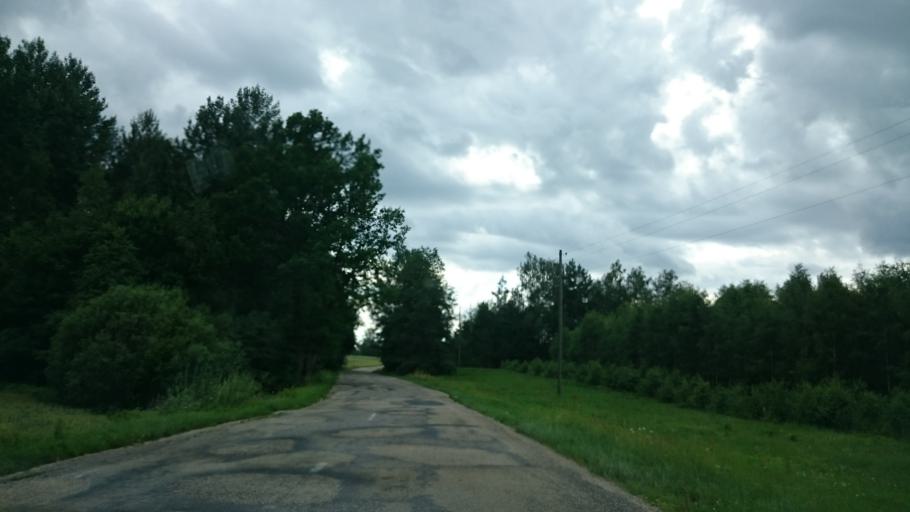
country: LV
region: Seja
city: Loja
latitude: 57.1991
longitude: 24.6259
